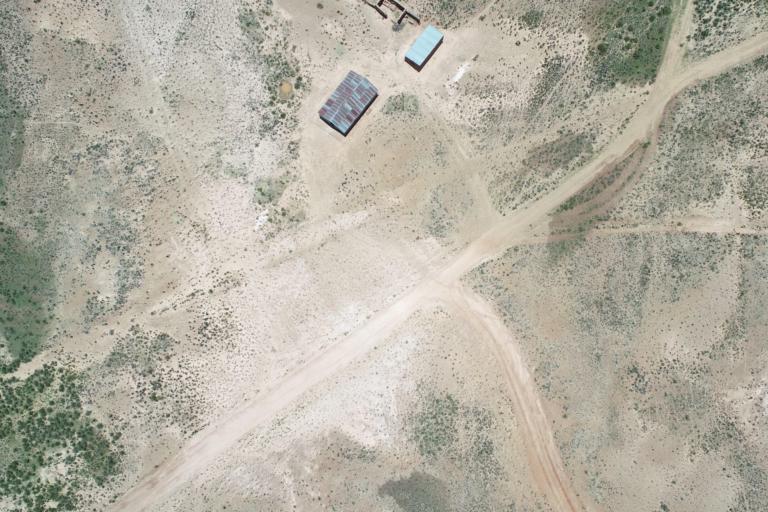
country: BO
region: La Paz
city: Curahuara de Carangas
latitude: -17.3065
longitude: -68.5067
